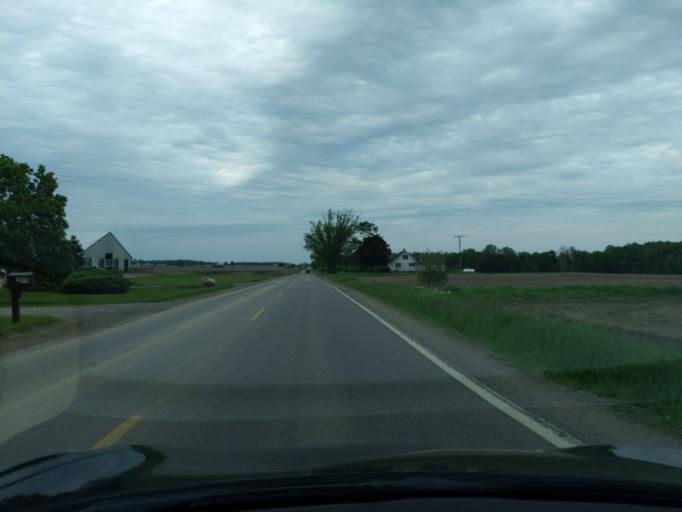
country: US
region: Michigan
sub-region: Ingham County
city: Mason
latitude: 42.6345
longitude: -84.3639
